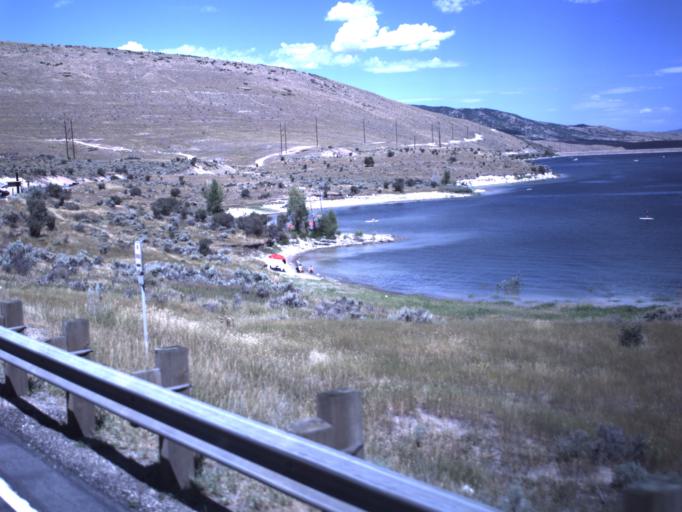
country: US
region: Utah
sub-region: Summit County
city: Oakley
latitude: 40.7710
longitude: -111.4054
